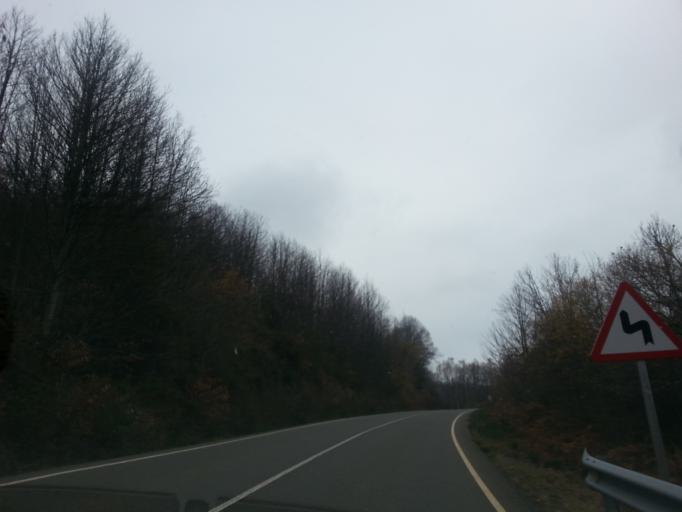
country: ES
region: Castille and Leon
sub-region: Provincia de Salamanca
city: Madronal
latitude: 40.4693
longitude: -6.0795
